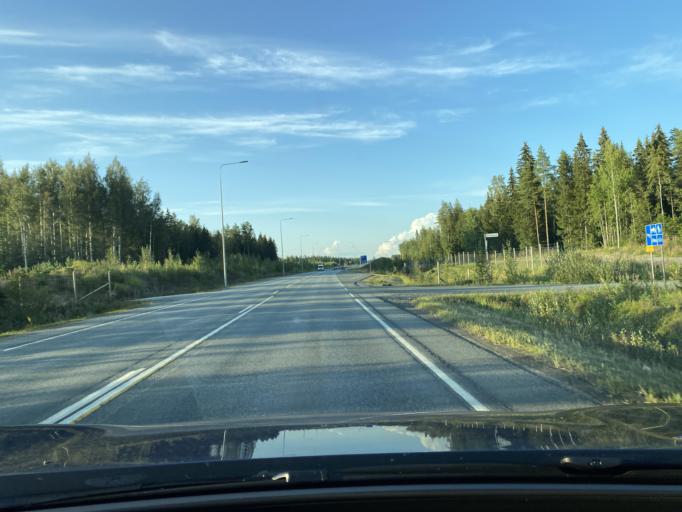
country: FI
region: Southern Ostrobothnia
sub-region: Seinaejoki
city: Seinaejoki
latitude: 62.6841
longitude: 22.8006
